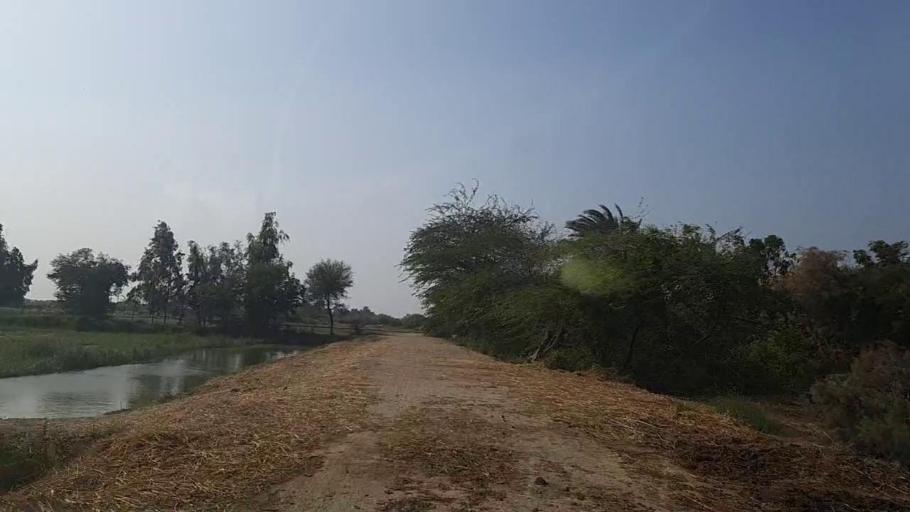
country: PK
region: Sindh
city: Mirpur Sakro
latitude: 24.5680
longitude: 67.8184
